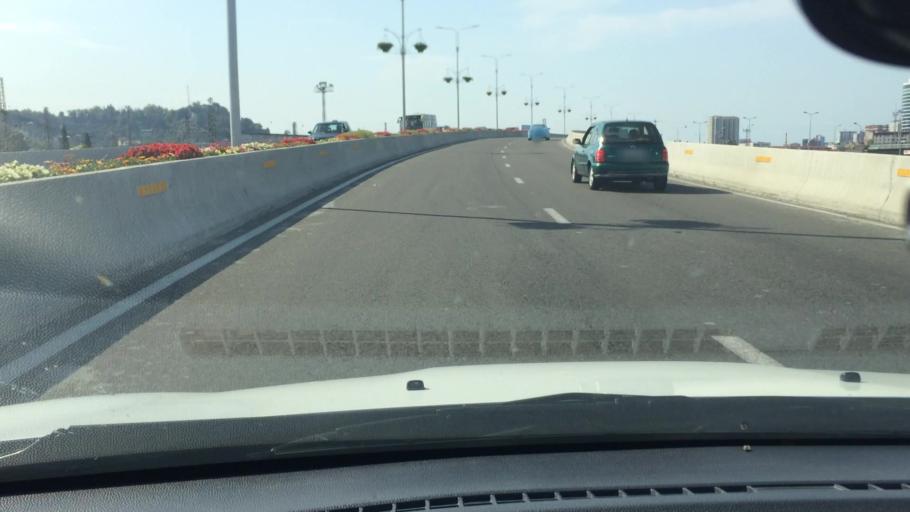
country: GE
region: Ajaria
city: Batumi
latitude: 41.6476
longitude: 41.6609
